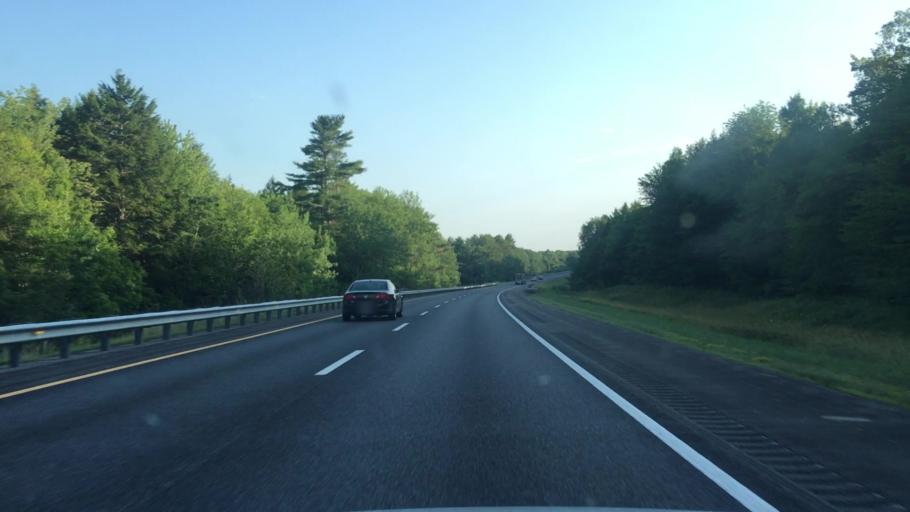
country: US
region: Maine
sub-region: Sagadahoc County
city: Richmond
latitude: 44.0460
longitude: -69.8957
